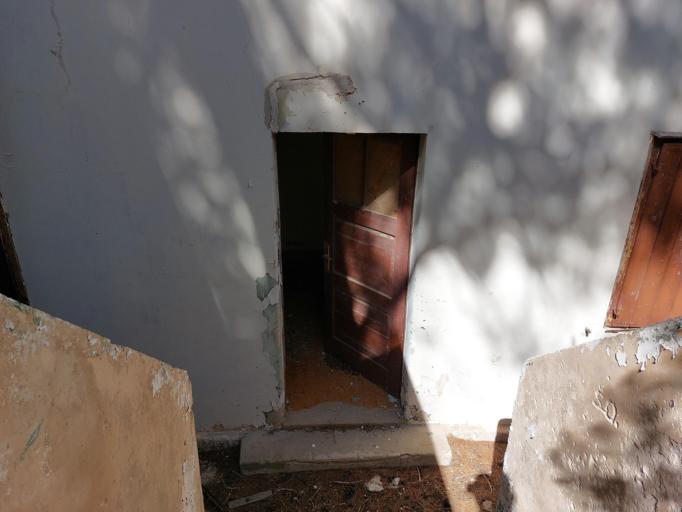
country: HR
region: Dubrovacko-Neretvanska
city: Smokvica
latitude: 42.7322
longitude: 16.8404
